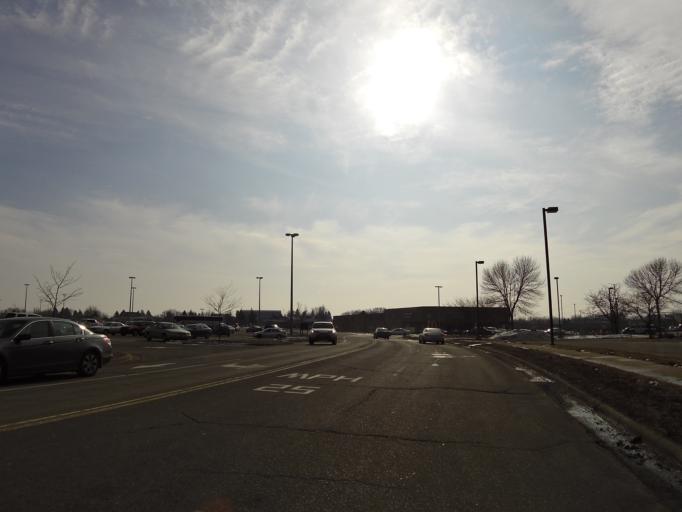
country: US
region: Minnesota
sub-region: Hennepin County
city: Eden Prairie
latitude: 44.8545
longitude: -93.4286
